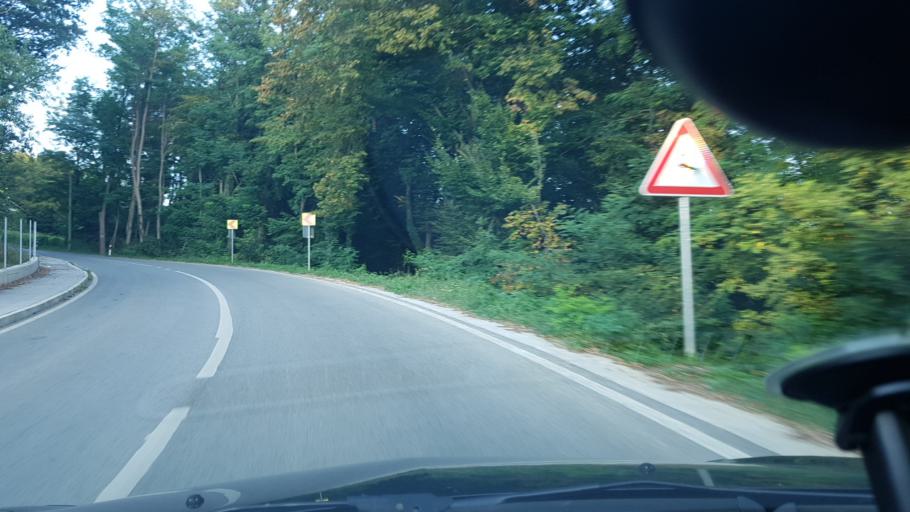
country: HR
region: Krapinsko-Zagorska
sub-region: Grad Krapina
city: Krapina
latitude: 46.1620
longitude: 15.8173
